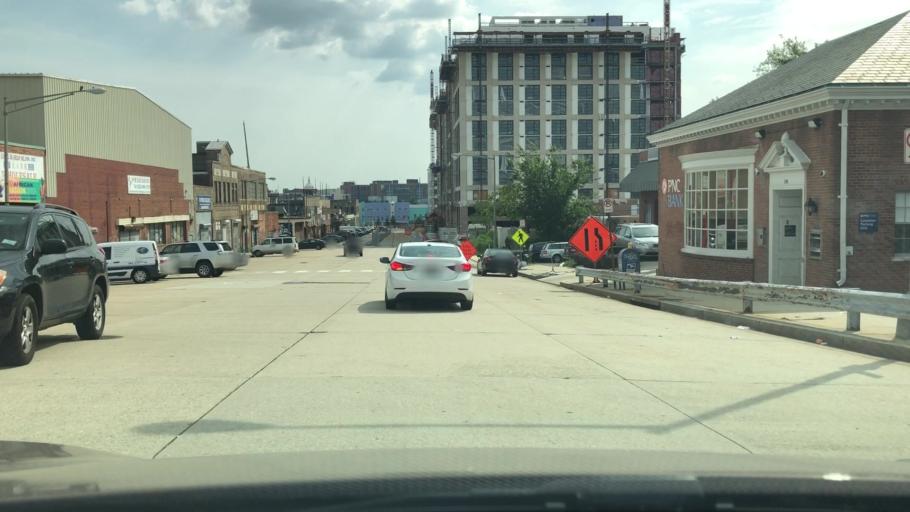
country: US
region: Washington, D.C.
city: Washington, D.C.
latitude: 38.9102
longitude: -76.9984
